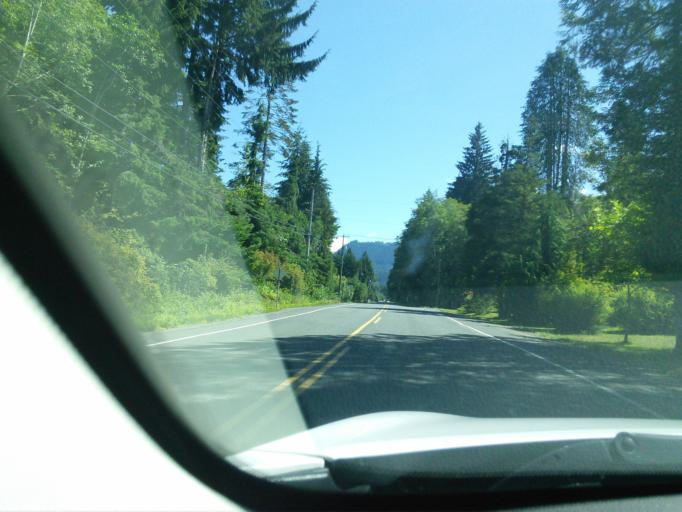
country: CA
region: British Columbia
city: Campbell River
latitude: 50.3183
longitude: -125.9225
